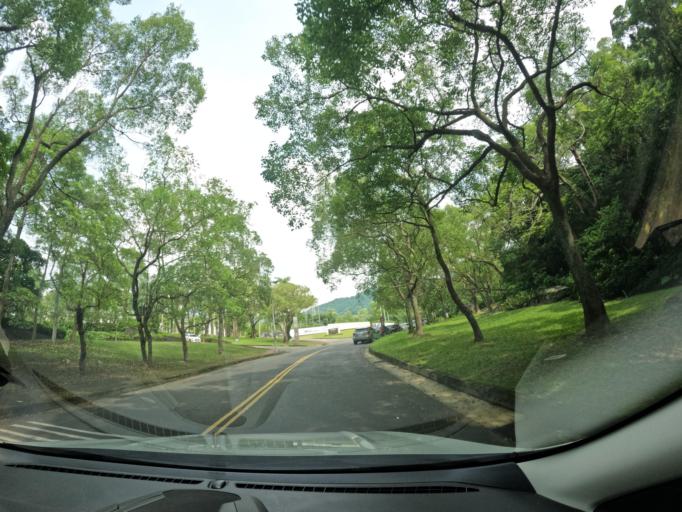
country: TW
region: Taiwan
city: Daxi
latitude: 24.8819
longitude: 121.3248
